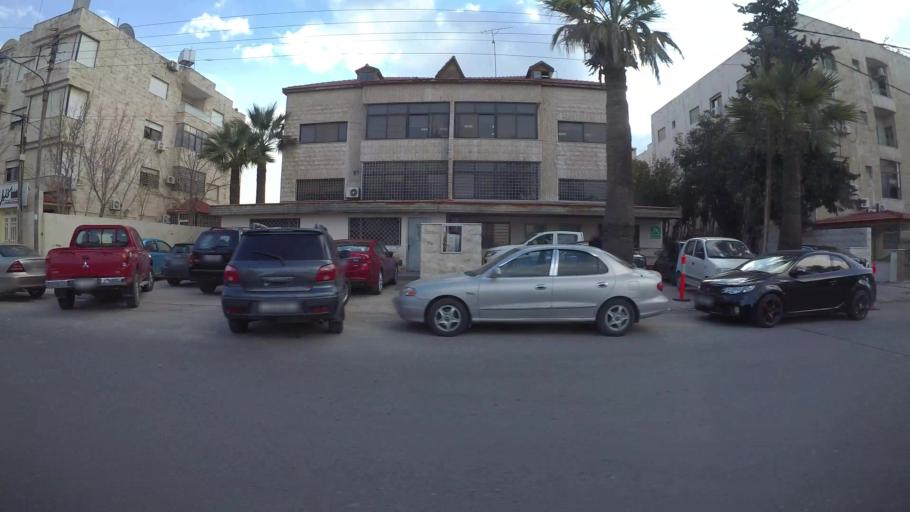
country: JO
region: Amman
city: Al Jubayhah
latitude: 31.9803
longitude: 35.8579
